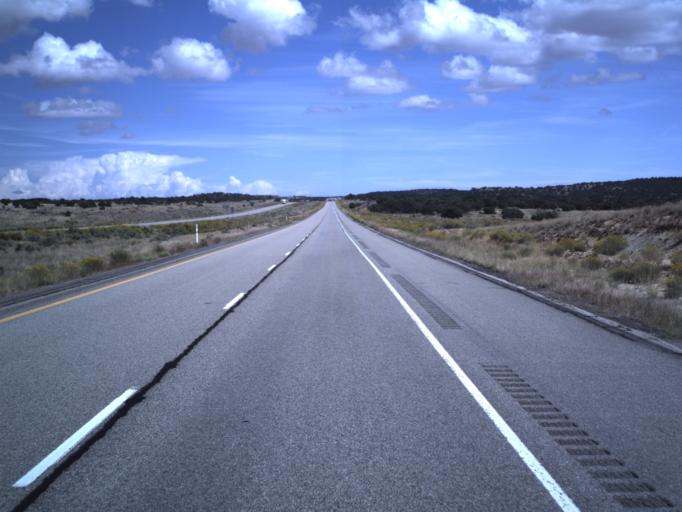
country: US
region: Utah
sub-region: Emery County
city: Castle Dale
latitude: 38.8700
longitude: -110.7704
